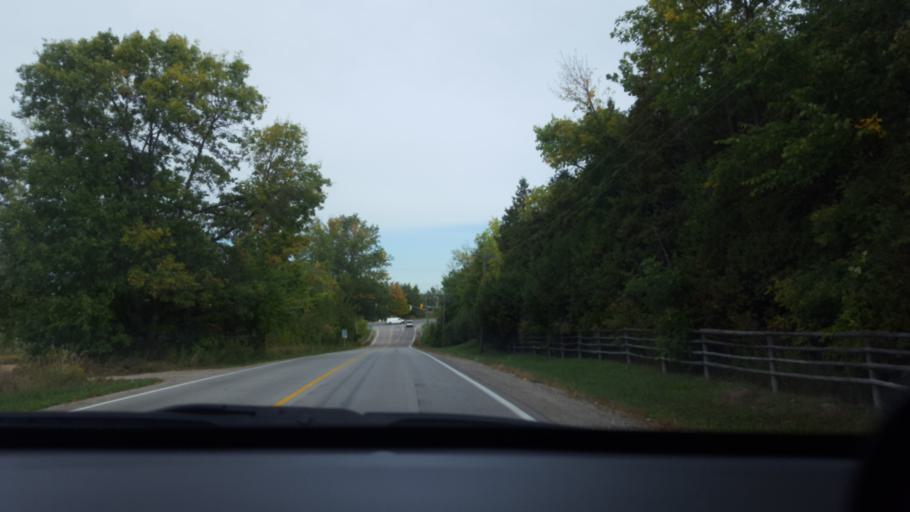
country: CA
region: Ontario
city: Newmarket
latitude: 44.0358
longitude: -79.5559
